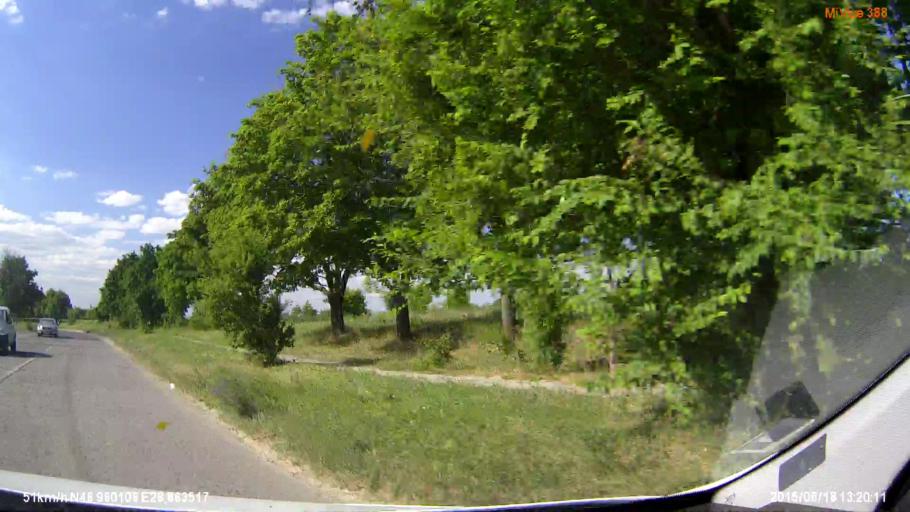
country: MD
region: Chisinau
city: Chisinau
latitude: 46.9600
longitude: 28.8636
